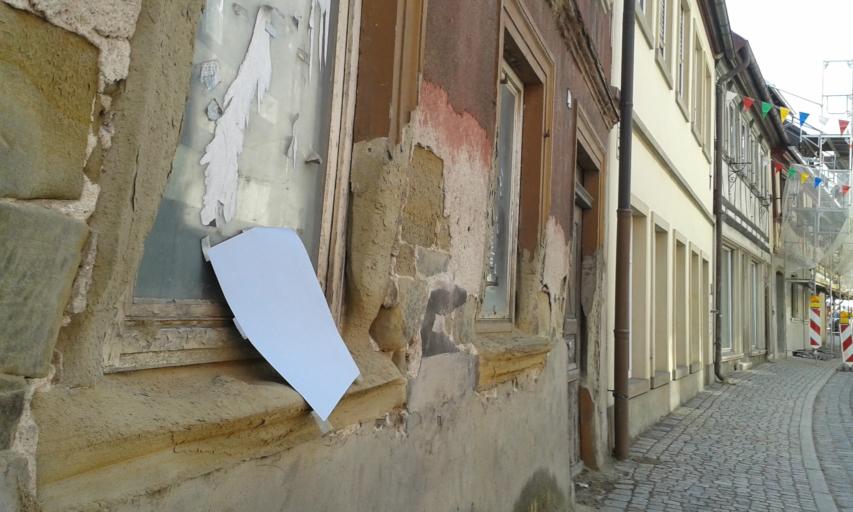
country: DE
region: Bavaria
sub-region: Regierungsbezirk Unterfranken
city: Zeil
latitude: 50.0084
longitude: 10.5951
